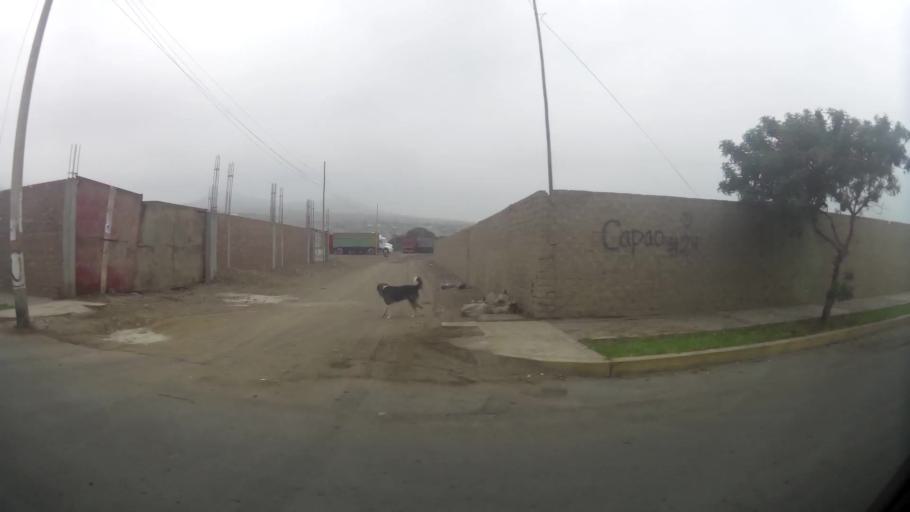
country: PE
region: Lima
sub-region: Provincia de Huaral
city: Chancay
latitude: -11.5725
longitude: -77.2685
